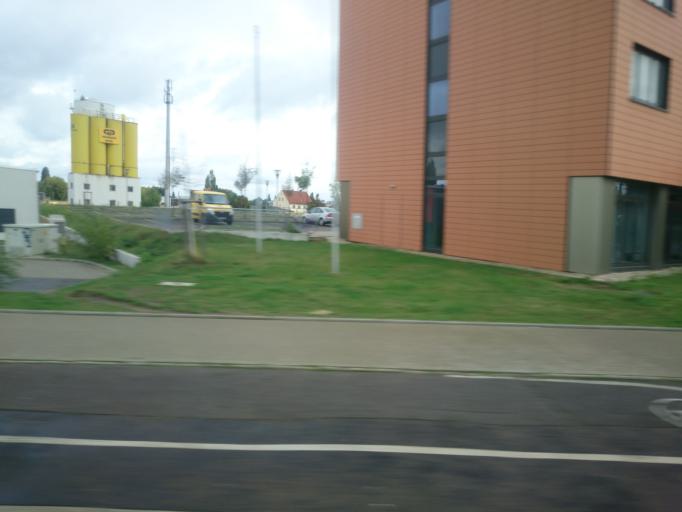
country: DE
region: Saxony-Anhalt
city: Halle (Saale)
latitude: 51.4891
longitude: 11.9951
